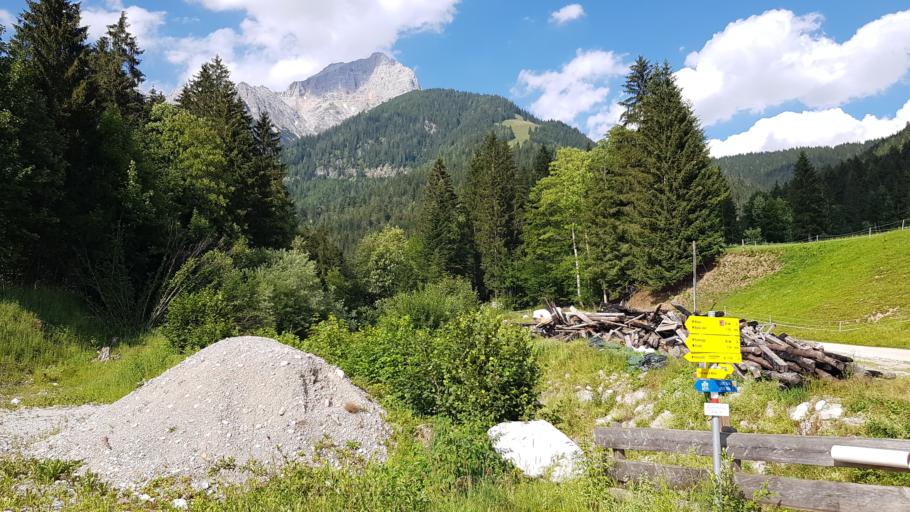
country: AT
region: Salzburg
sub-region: Politischer Bezirk Zell am See
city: Maria Alm am Steinernen Meer
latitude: 47.4183
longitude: 12.9296
